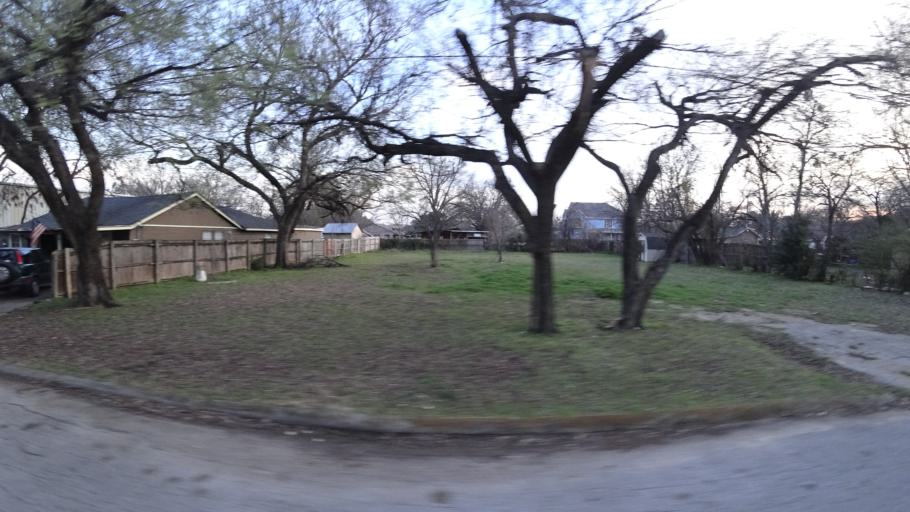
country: US
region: Texas
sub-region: Denton County
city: Lewisville
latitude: 33.0429
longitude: -96.9959
